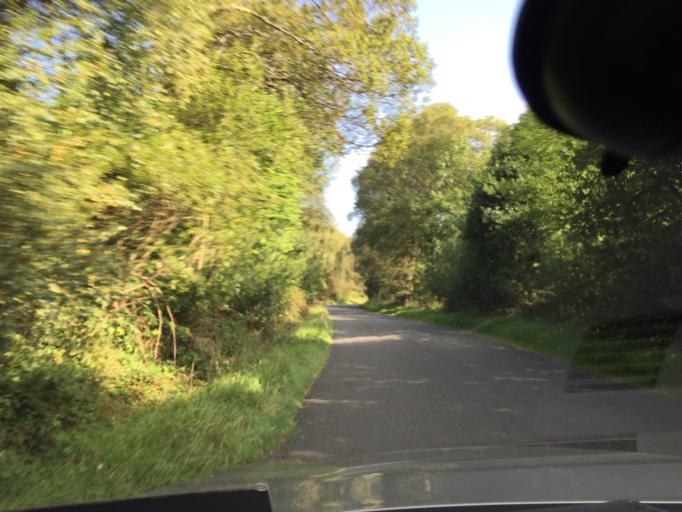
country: IE
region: Leinster
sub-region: Wicklow
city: Rathdrum
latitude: 53.0330
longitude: -6.3153
